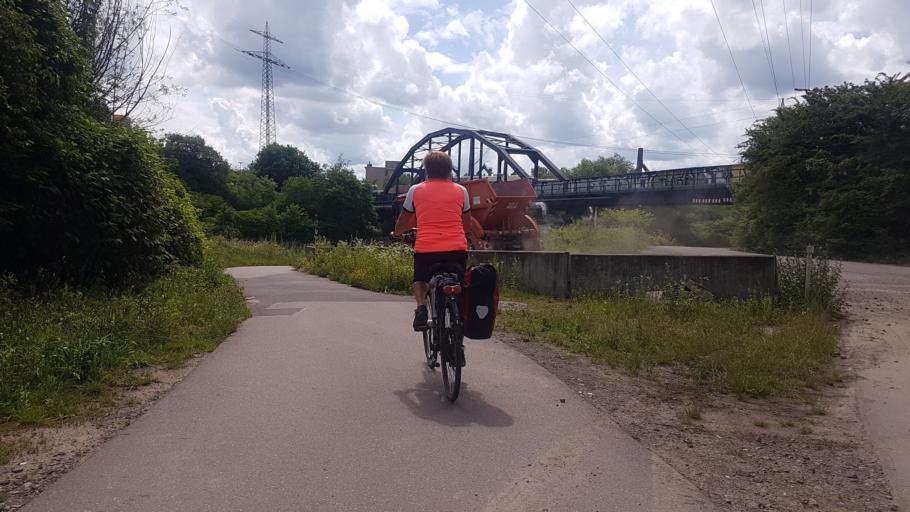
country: DE
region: Saarland
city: Volklingen
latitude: 49.2542
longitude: 6.8395
